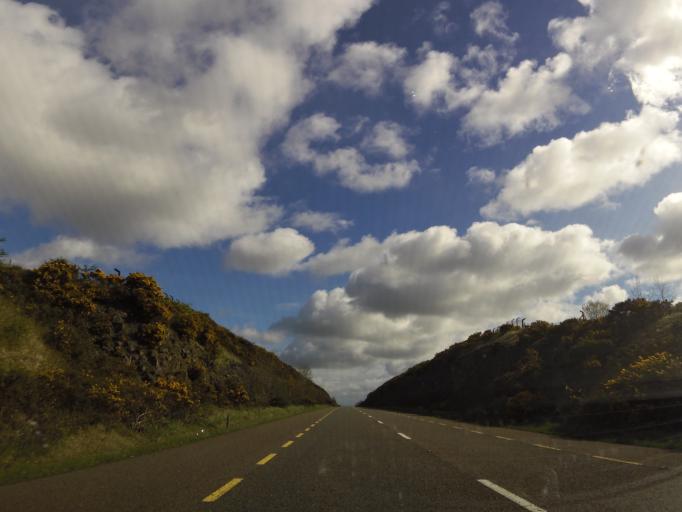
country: IE
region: Connaught
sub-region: Maigh Eo
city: Kiltamagh
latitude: 53.7888
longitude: -8.9360
